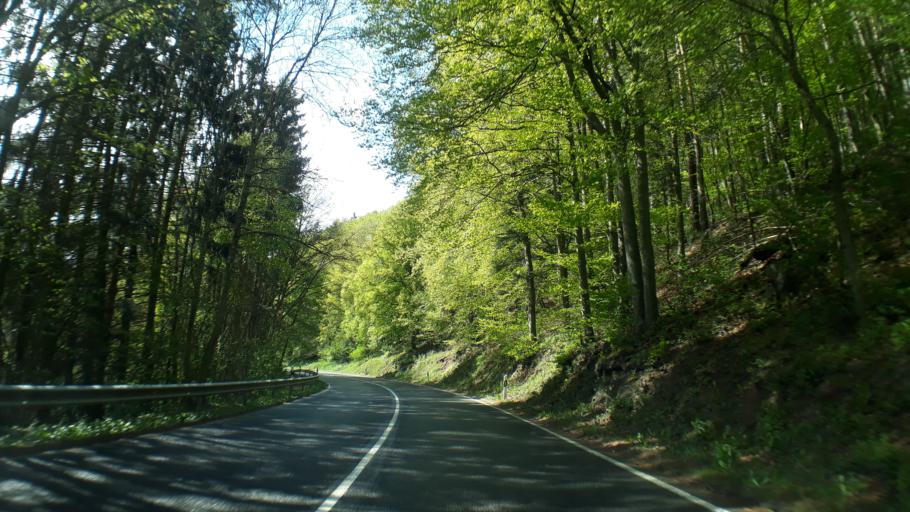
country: DE
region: North Rhine-Westphalia
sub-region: Regierungsbezirk Koln
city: Kall
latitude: 50.5144
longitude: 6.5793
